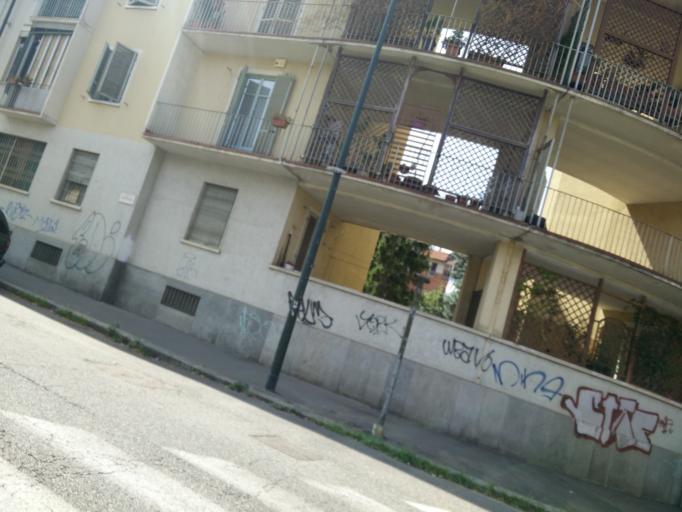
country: IT
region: Piedmont
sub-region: Provincia di Torino
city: Moncalieri
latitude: 45.0326
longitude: 7.6718
